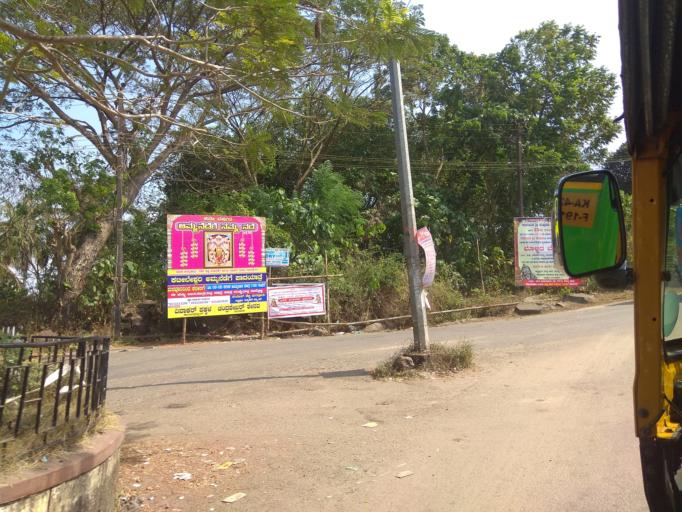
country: IN
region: Karnataka
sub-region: Dakshina Kannada
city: Mangalore
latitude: 12.9418
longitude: 74.8541
